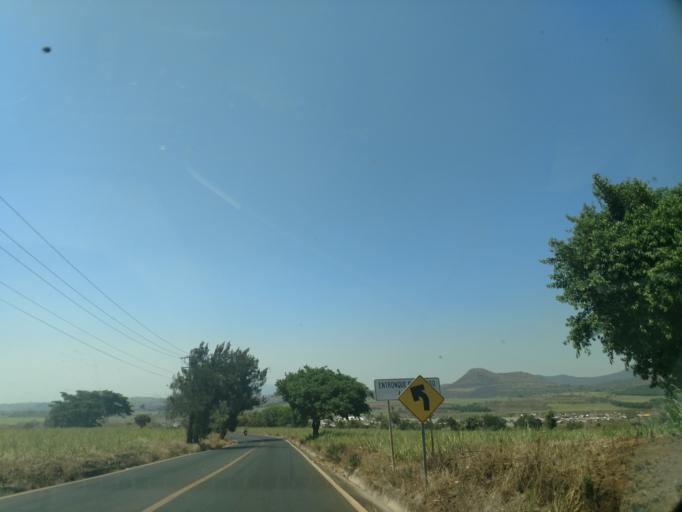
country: MX
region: Nayarit
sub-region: Tepic
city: La Corregidora
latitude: 21.4899
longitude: -104.7929
